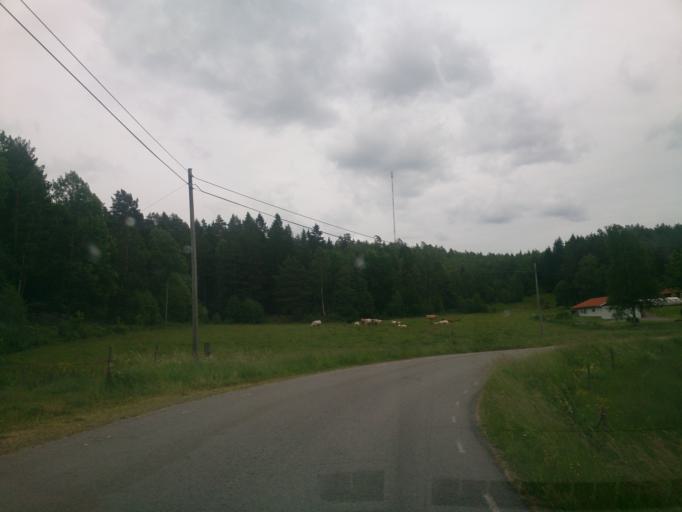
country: SE
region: OEstergoetland
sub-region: Atvidabergs Kommun
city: Atvidaberg
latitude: 58.3097
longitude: 16.0762
